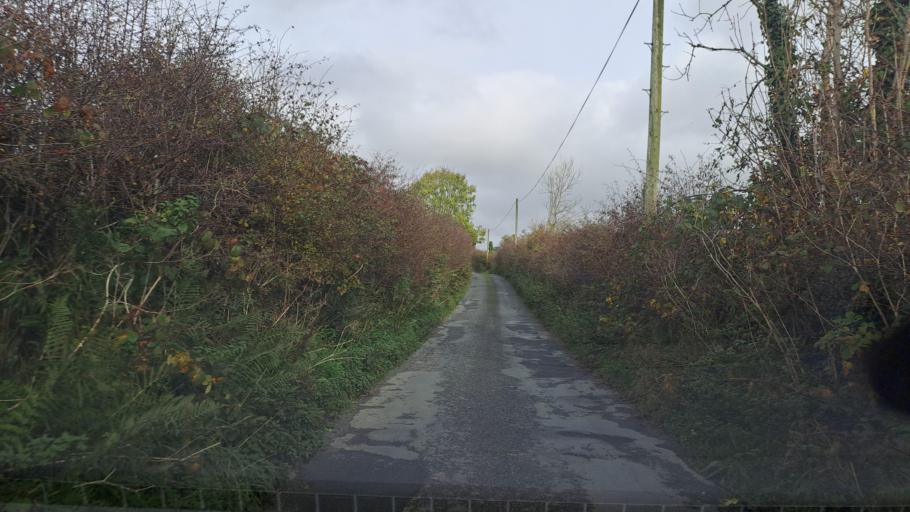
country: IE
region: Ulster
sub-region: County Monaghan
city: Carrickmacross
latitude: 53.9999
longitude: -6.7813
